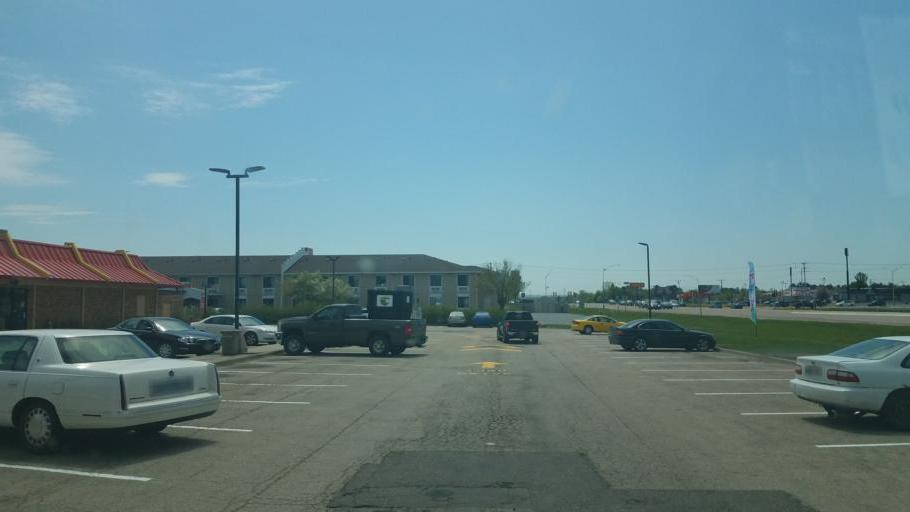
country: US
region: Wisconsin
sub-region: Monroe County
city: Tomah
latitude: 44.0198
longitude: -90.5046
